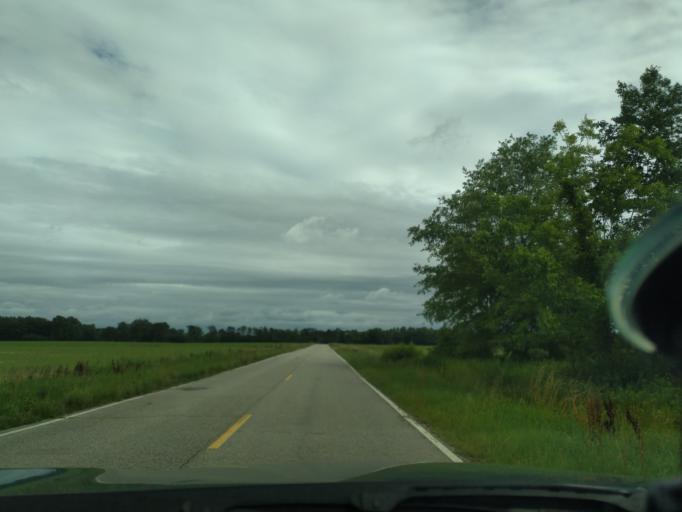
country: US
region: North Carolina
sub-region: Washington County
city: Plymouth
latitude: 35.8799
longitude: -76.7092
